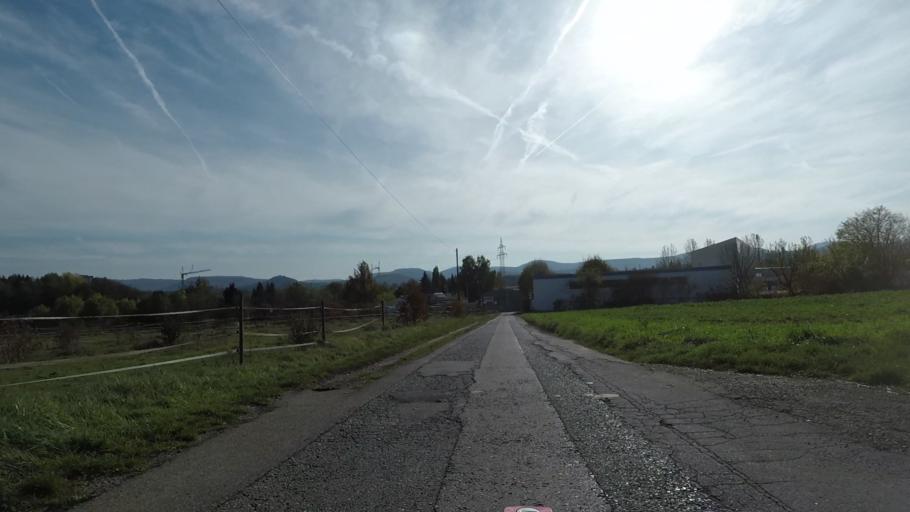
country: DE
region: Baden-Wuerttemberg
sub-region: Tuebingen Region
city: Wannweil
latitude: 48.5011
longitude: 9.1547
